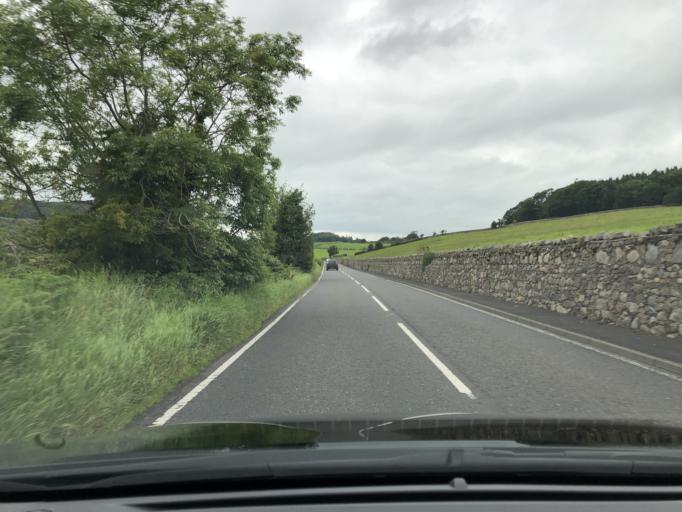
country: GB
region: Northern Ireland
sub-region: Down District
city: Castlewellan
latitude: 54.2560
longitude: -5.9604
